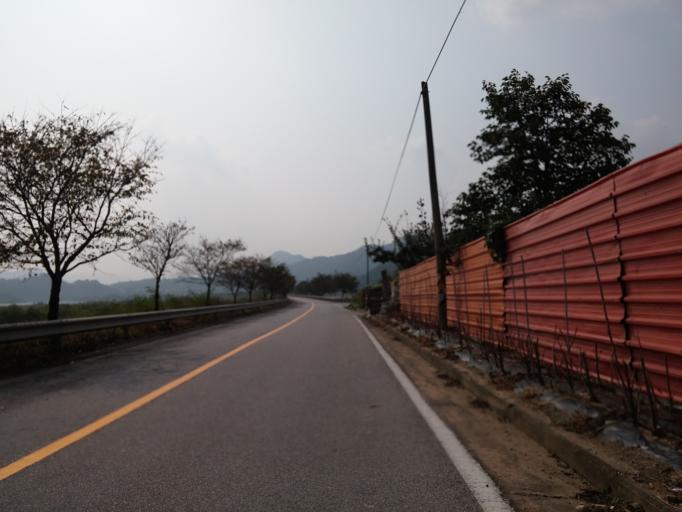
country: KR
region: Chungcheongbuk-do
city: Yong-dong
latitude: 36.3368
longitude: 127.7751
